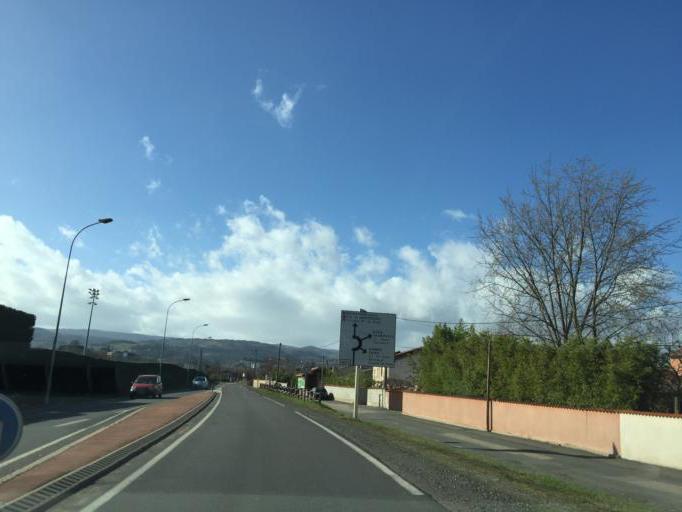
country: FR
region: Rhone-Alpes
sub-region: Departement de la Loire
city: Savigneux
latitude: 45.6127
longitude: 4.0782
